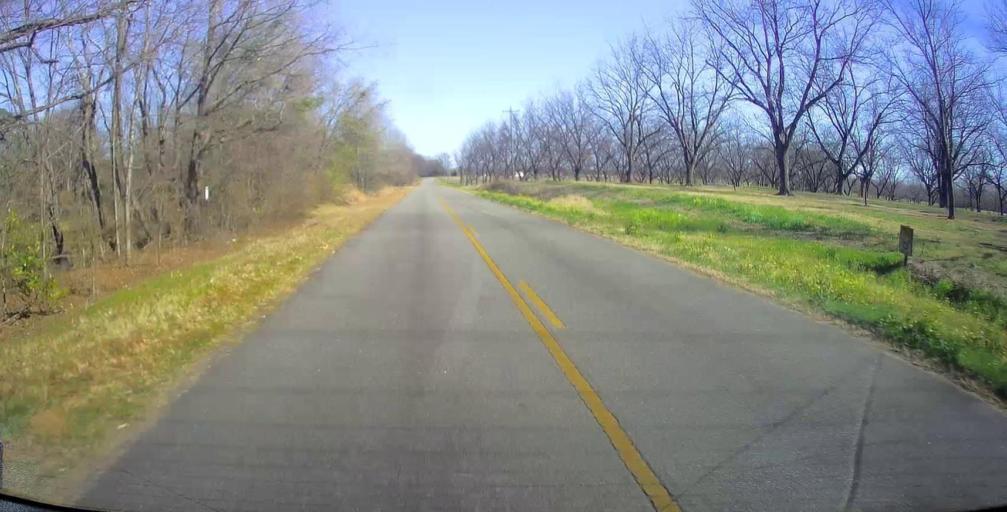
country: US
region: Georgia
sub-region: Peach County
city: Fort Valley
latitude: 32.6294
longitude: -83.8456
